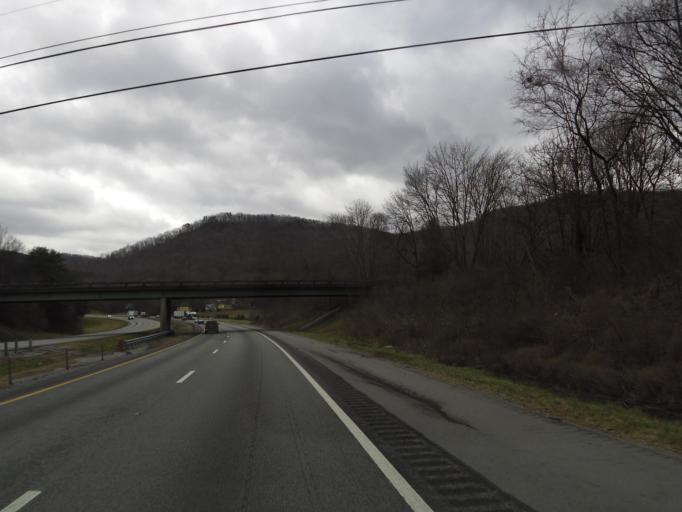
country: US
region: Georgia
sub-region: Dade County
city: Trenton
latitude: 34.9915
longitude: -85.5093
